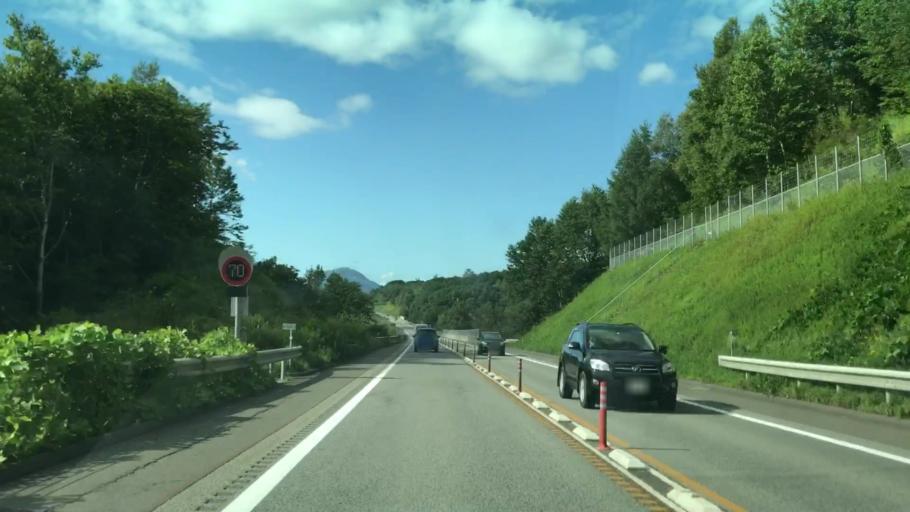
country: JP
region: Hokkaido
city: Date
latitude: 42.4306
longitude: 140.9251
